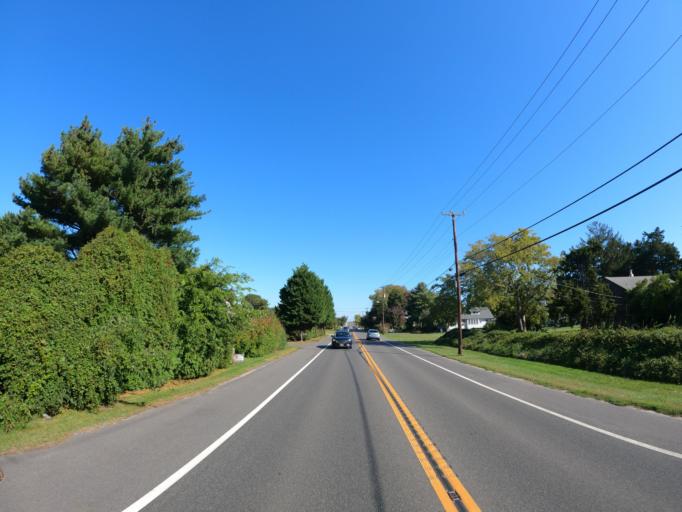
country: US
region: New Jersey
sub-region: Cape May County
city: West Cape May
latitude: 38.9546
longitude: -74.9250
